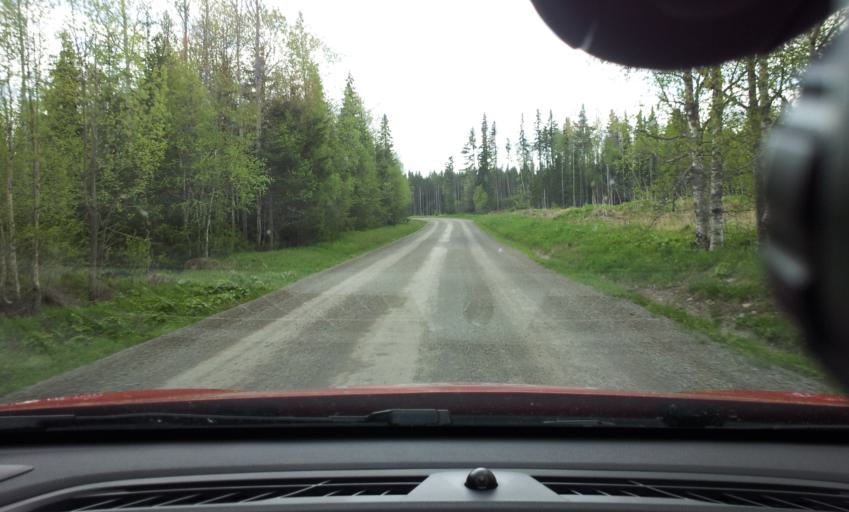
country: SE
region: Jaemtland
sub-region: OEstersunds Kommun
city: Ostersund
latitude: 63.1315
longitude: 14.5304
